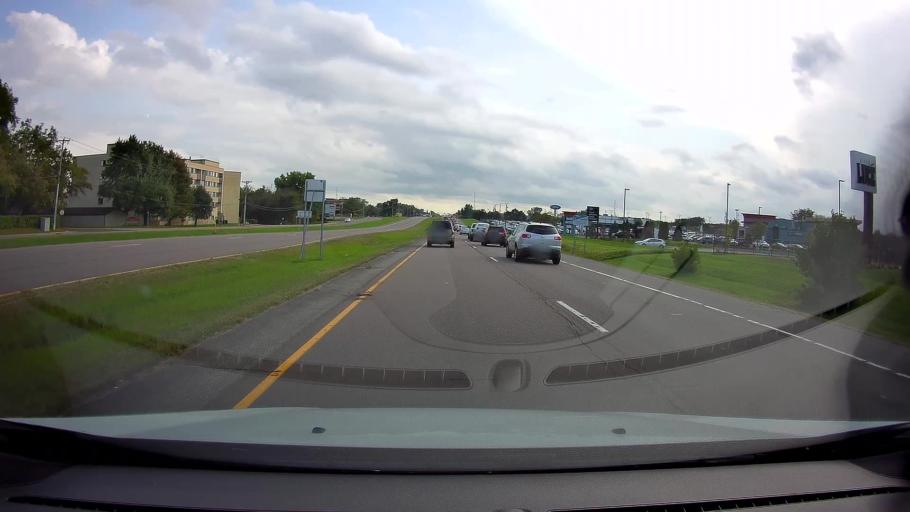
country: US
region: Minnesota
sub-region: Ramsey County
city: Roseville
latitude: 45.0271
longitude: -93.1672
